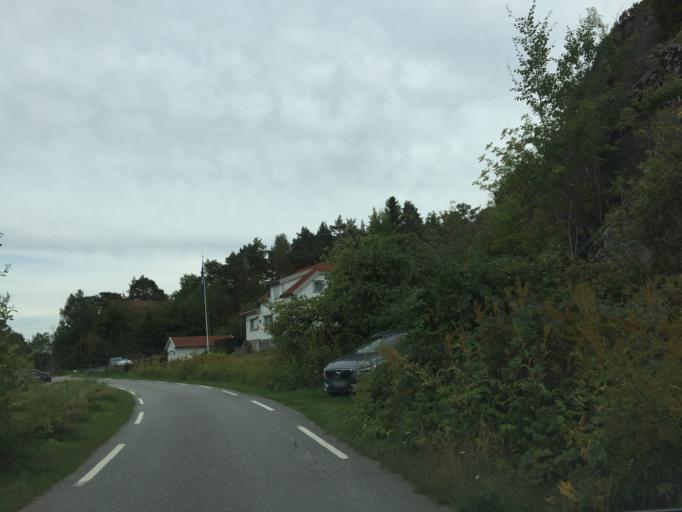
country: NO
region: Ostfold
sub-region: Hvaler
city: Skjaerhalden
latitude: 59.0380
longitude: 11.0515
